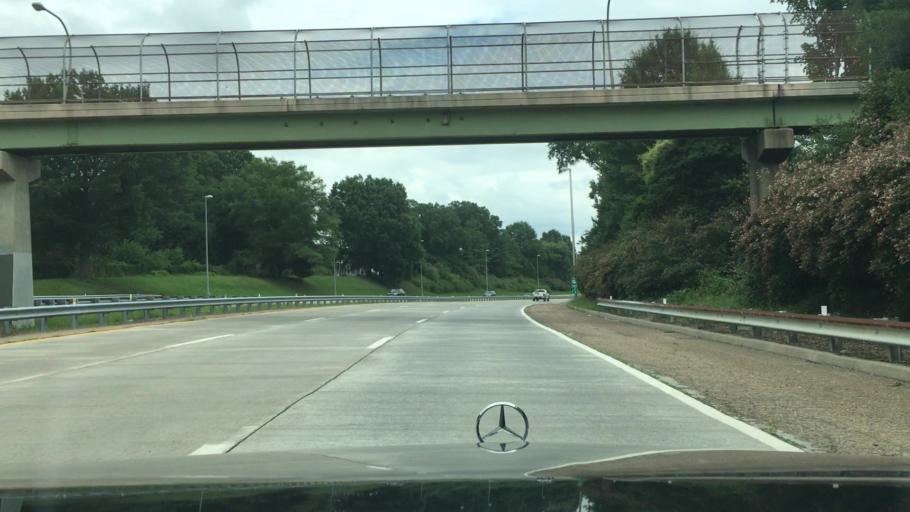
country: US
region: Virginia
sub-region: City of Richmond
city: Richmond
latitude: 37.5478
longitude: -77.4711
